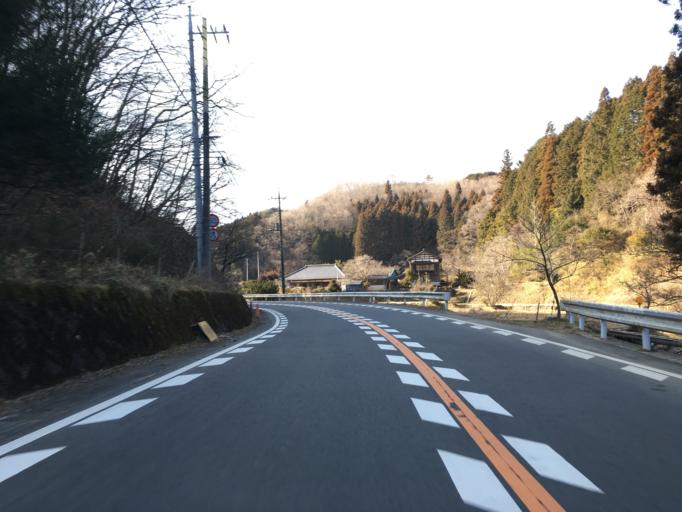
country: JP
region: Ibaraki
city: Takahagi
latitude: 36.7425
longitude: 140.5959
